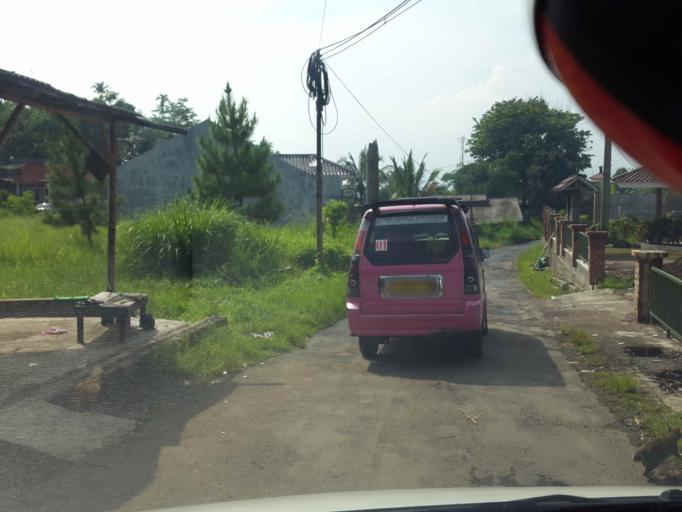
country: ID
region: West Java
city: Sukabumi
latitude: -6.9121
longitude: 106.9712
